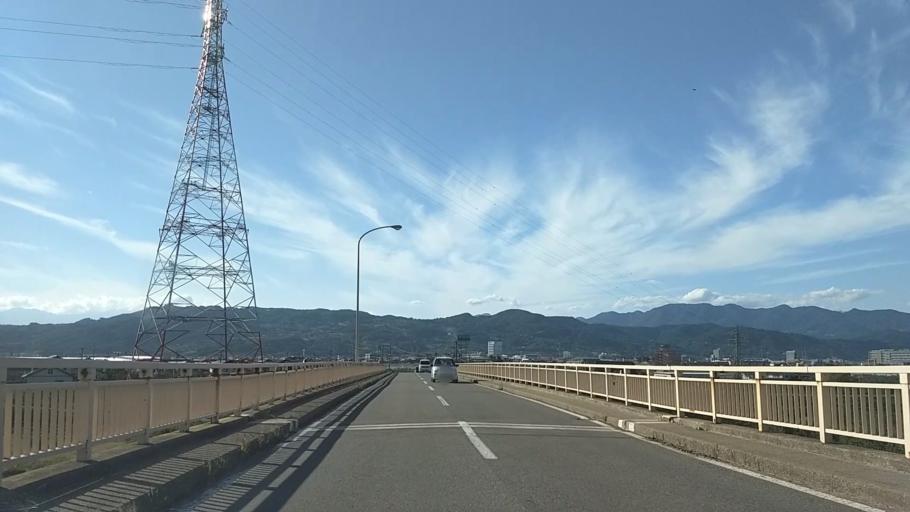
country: JP
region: Nagano
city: Nagano-shi
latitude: 36.5631
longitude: 138.1554
